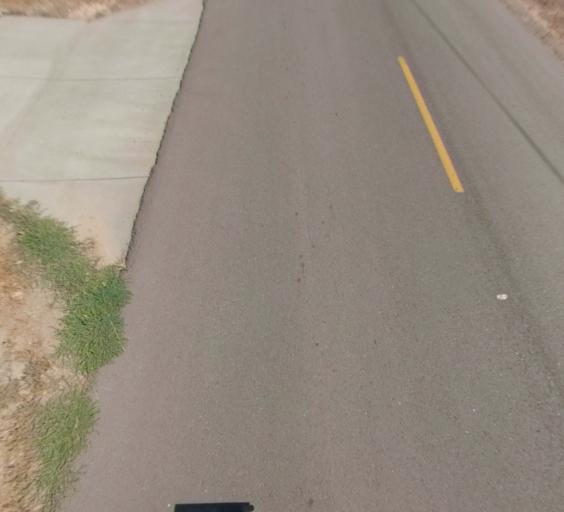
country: US
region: California
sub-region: Madera County
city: Bonadelle Ranchos-Madera Ranchos
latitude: 36.9929
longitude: -119.8793
